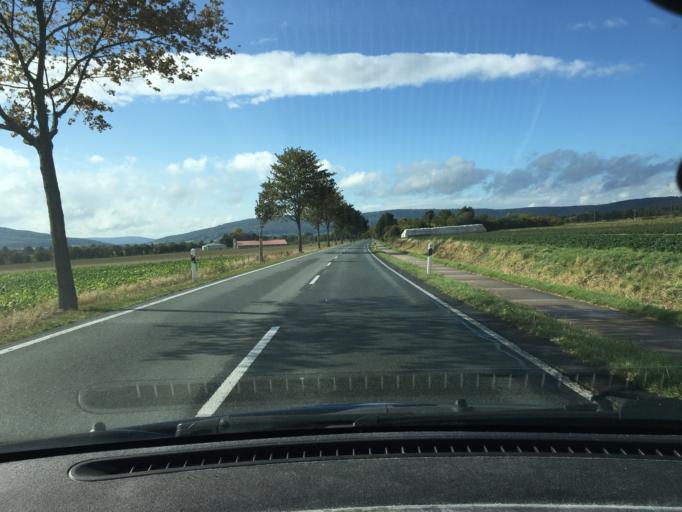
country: DE
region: Lower Saxony
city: Springe
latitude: 52.2107
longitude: 9.6094
